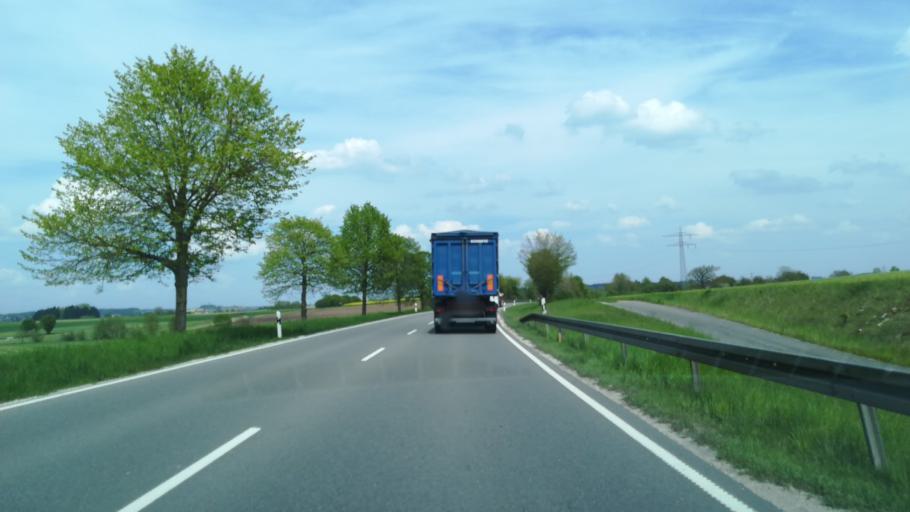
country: DE
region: Baden-Wuerttemberg
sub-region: Tuebingen Region
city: Messkirch
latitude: 47.9961
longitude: 9.0859
